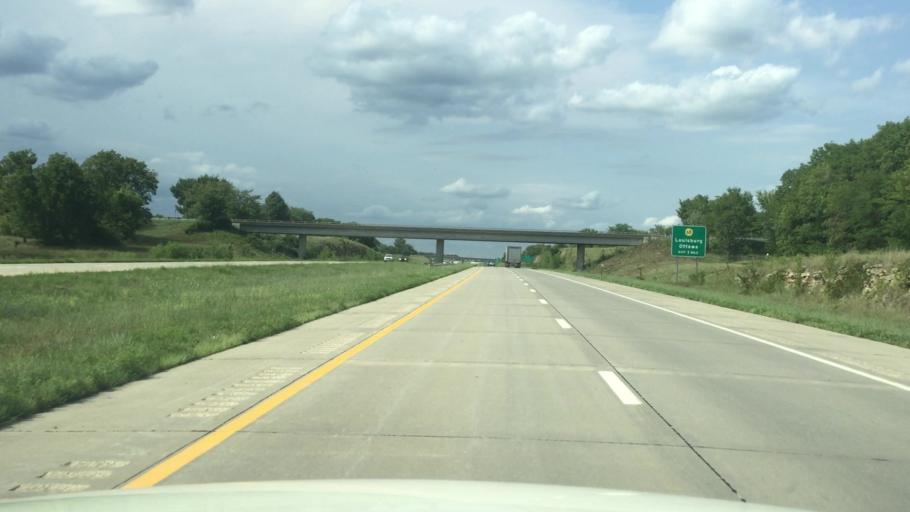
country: US
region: Kansas
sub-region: Miami County
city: Louisburg
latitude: 38.6049
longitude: -94.6940
